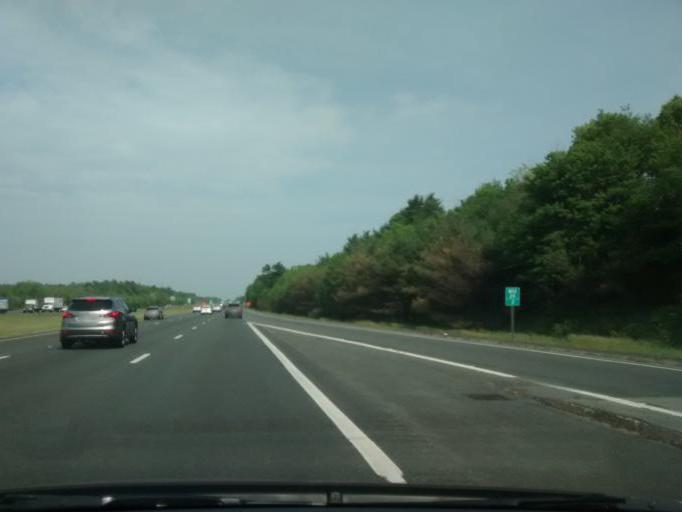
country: US
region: Massachusetts
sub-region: Bristol County
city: Raynham
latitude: 41.9619
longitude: -71.1185
